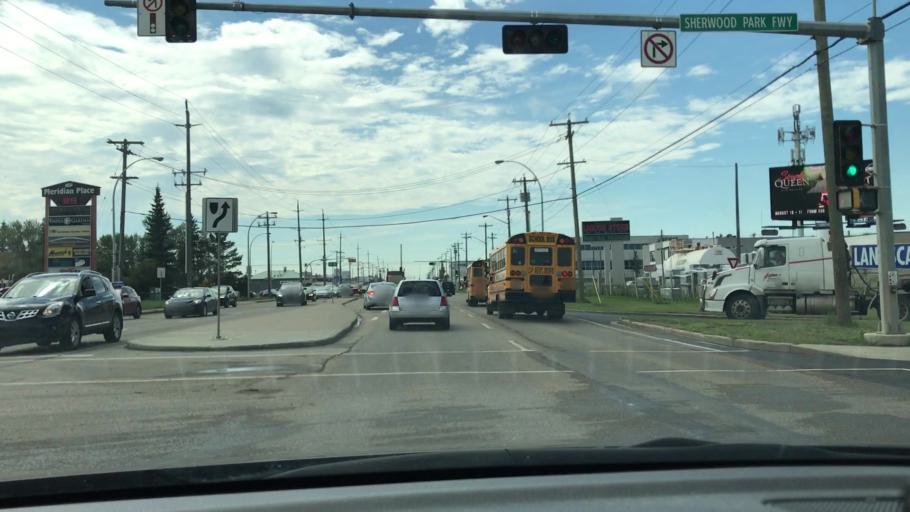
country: CA
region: Alberta
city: Edmonton
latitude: 53.5139
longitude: -113.4185
